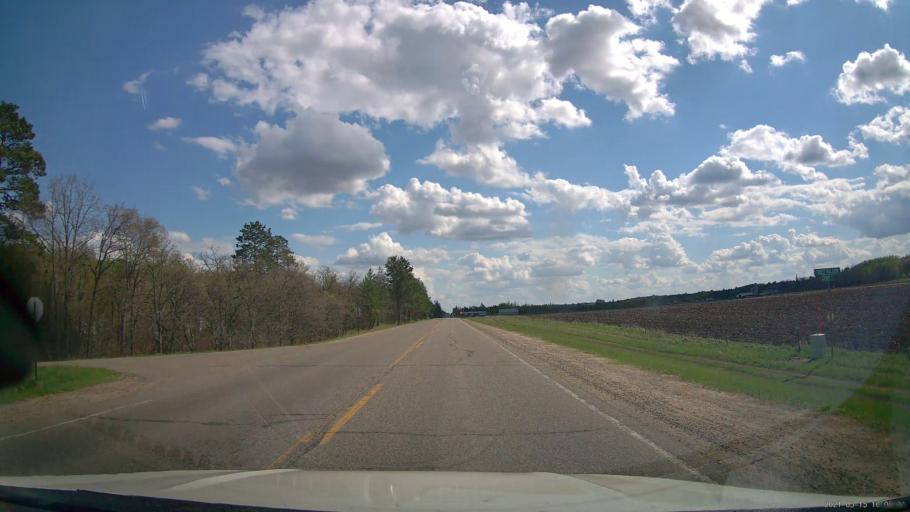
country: US
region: Minnesota
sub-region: Hubbard County
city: Park Rapids
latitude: 46.9632
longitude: -94.9526
